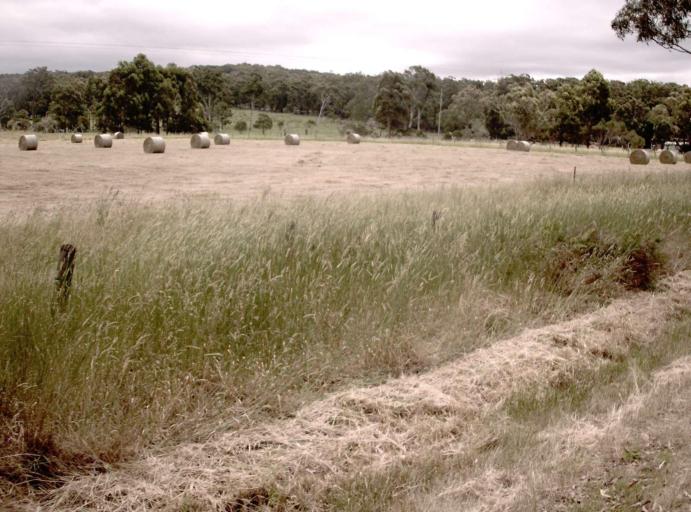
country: AU
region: Victoria
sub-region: Latrobe
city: Traralgon
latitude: -38.5106
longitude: 146.6493
